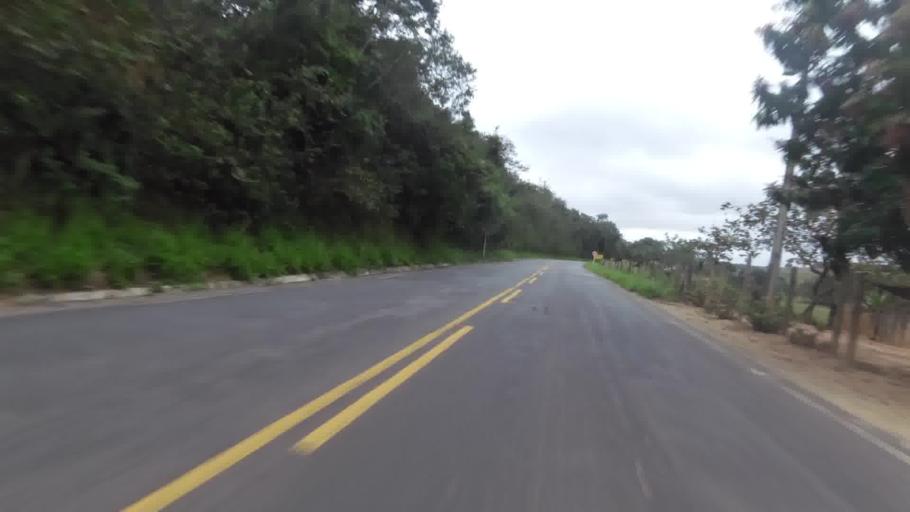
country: BR
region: Espirito Santo
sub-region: Alfredo Chaves
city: Alfredo Chaves
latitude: -20.6842
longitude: -40.7064
